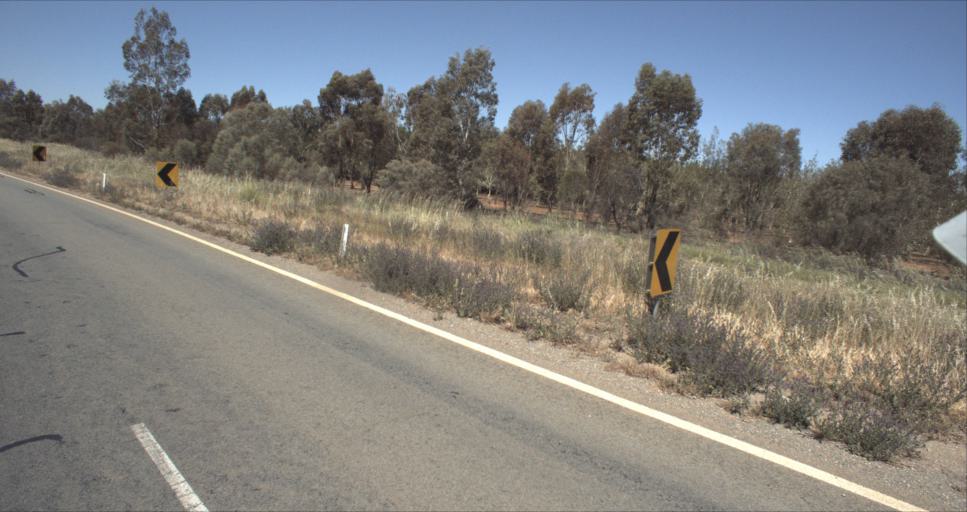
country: AU
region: New South Wales
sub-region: Leeton
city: Leeton
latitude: -34.5045
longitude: 146.4417
